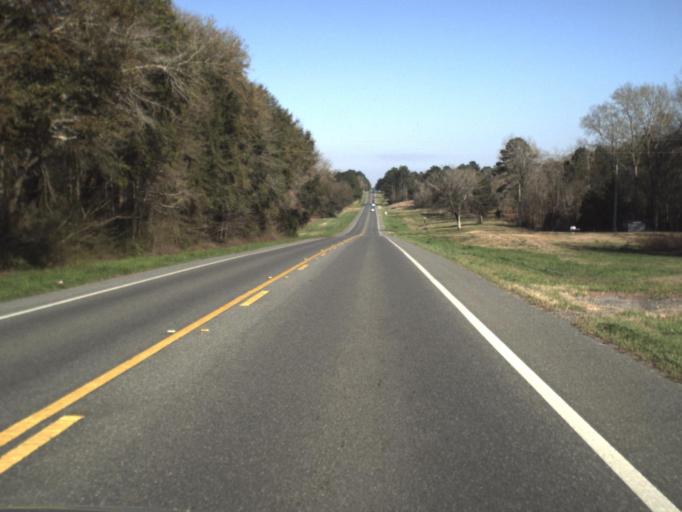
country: US
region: Florida
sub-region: Jackson County
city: Marianna
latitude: 30.7849
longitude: -85.3363
